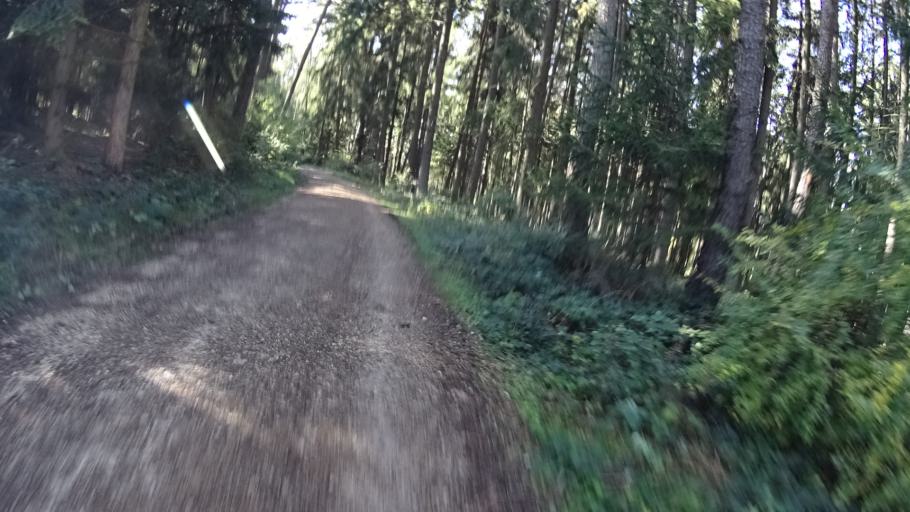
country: DE
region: Bavaria
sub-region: Upper Bavaria
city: Hitzhofen
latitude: 48.8490
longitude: 11.3439
